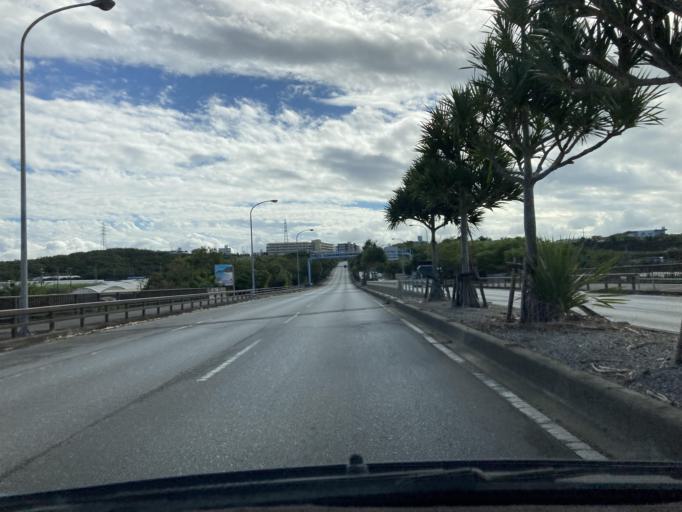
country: JP
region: Okinawa
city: Tomigusuku
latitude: 26.1691
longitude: 127.7262
